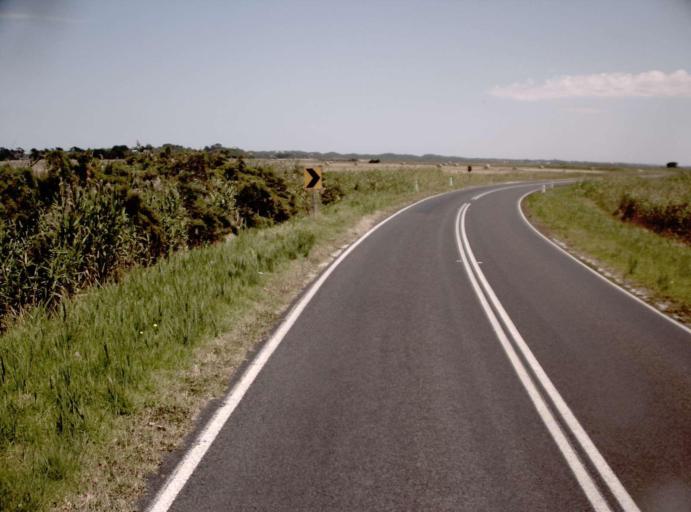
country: AU
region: Victoria
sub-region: Bass Coast
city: North Wonthaggi
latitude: -38.7004
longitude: 145.8490
